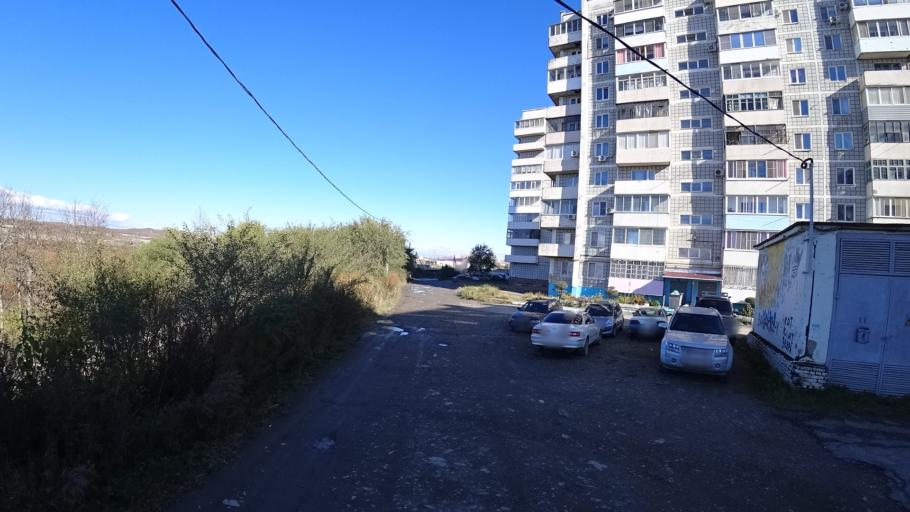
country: RU
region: Khabarovsk Krai
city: Amursk
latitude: 50.2189
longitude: 136.8933
